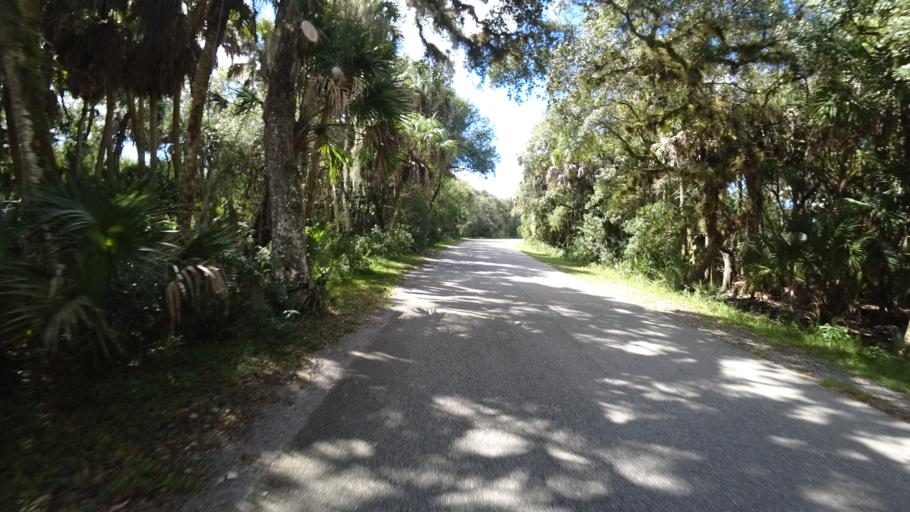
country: US
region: Florida
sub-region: Sarasota County
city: Lake Sarasota
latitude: 27.2456
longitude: -82.3049
